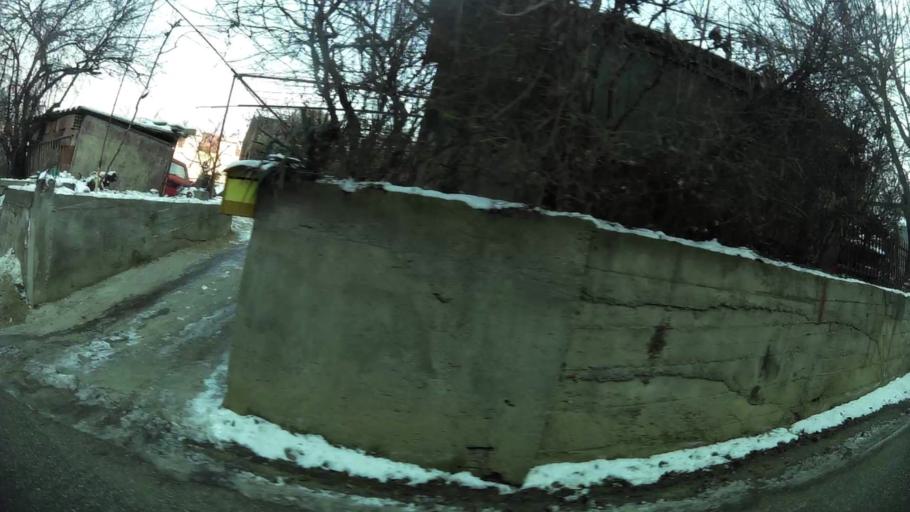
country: MK
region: Sopiste
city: Sopishte
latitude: 41.9723
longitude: 21.4351
